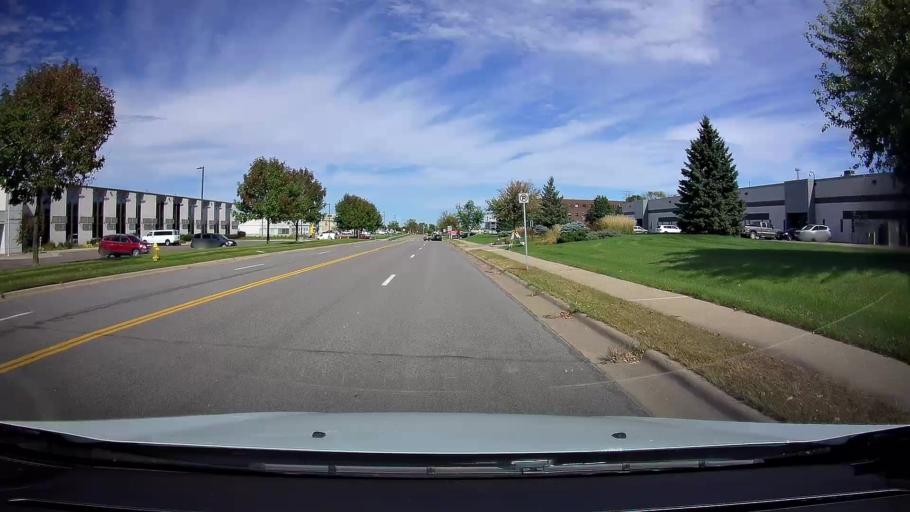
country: US
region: Minnesota
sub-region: Ramsey County
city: Roseville
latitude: 45.0139
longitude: -93.1820
